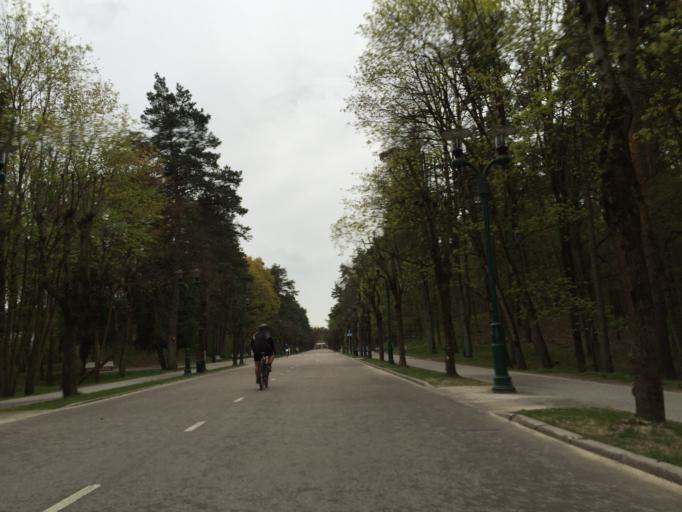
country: LV
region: Riga
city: Jaunciems
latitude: 57.0095
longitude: 24.1564
